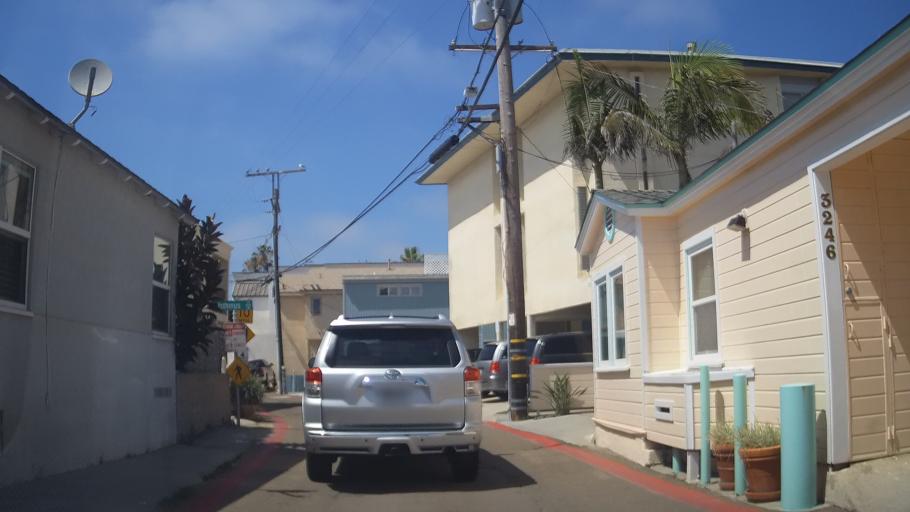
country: US
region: California
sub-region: San Diego County
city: La Jolla
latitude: 32.7730
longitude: -117.2500
